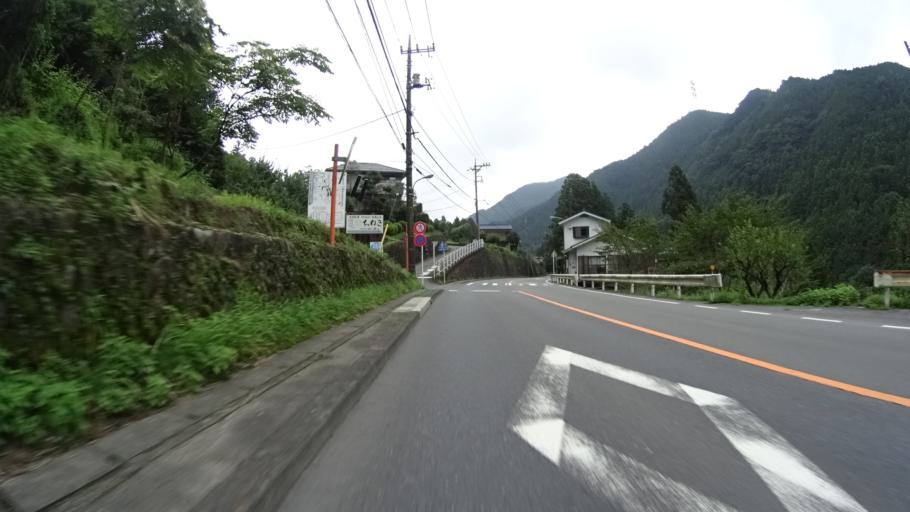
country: JP
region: Tokyo
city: Ome
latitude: 35.8065
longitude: 139.1683
